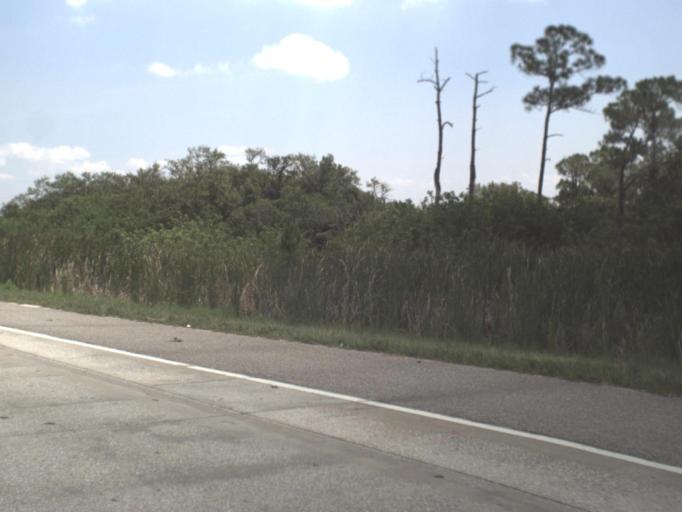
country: US
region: Florida
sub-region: Pinellas County
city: Feather Sound
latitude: 27.8850
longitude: -82.6529
